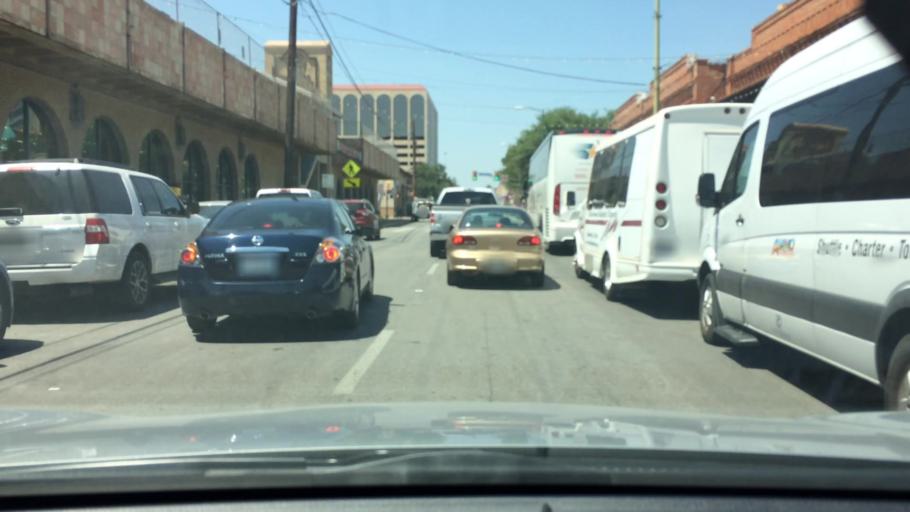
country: US
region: Texas
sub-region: Bexar County
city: San Antonio
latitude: 29.4248
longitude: -98.5003
